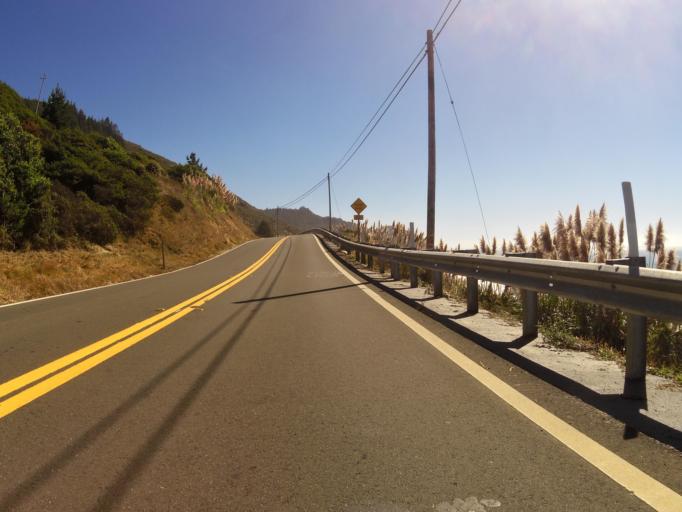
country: US
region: California
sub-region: Mendocino County
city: Fort Bragg
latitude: 39.6234
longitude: -123.7819
